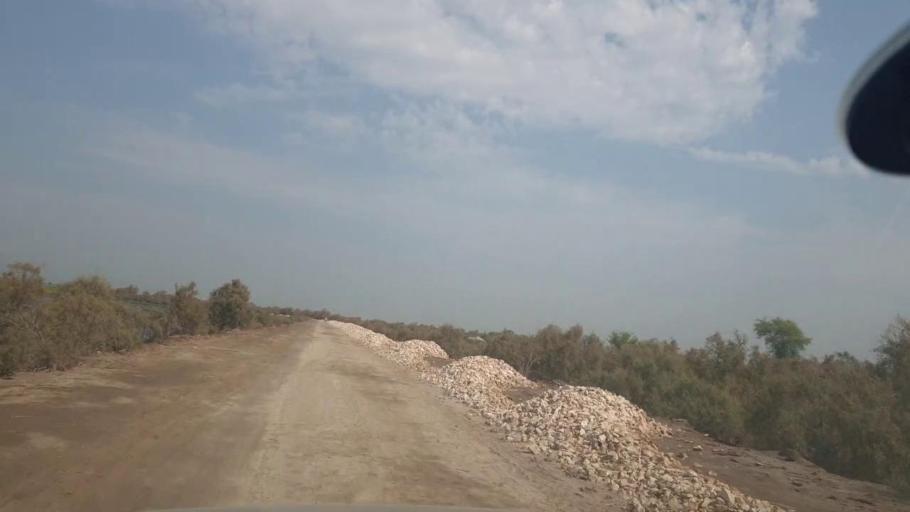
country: PK
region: Balochistan
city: Mehrabpur
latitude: 28.0914
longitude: 68.0959
